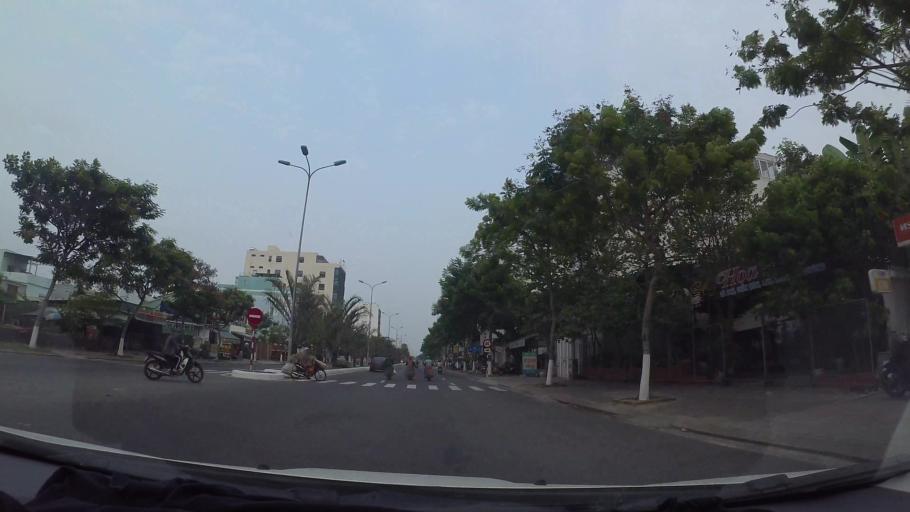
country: VN
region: Da Nang
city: Cam Le
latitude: 16.0316
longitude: 108.2130
